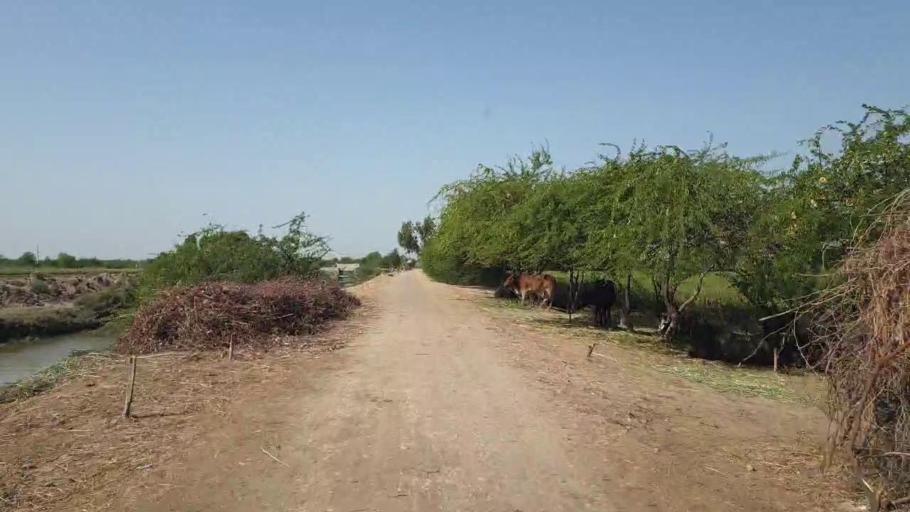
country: PK
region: Sindh
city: Tando Bago
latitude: 24.7428
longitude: 69.0661
